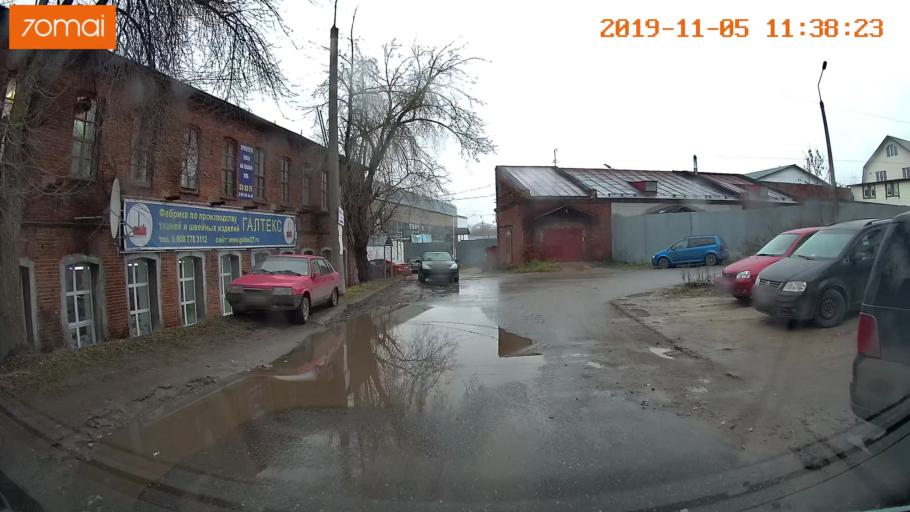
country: RU
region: Ivanovo
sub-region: Gorod Ivanovo
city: Ivanovo
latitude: 57.0108
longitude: 40.9583
